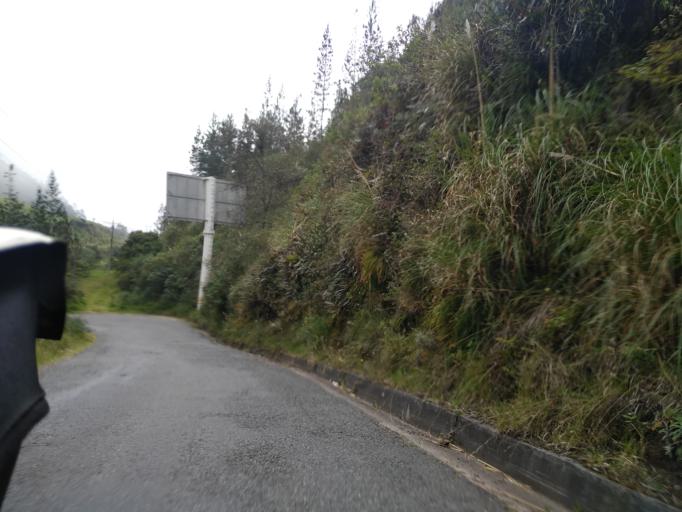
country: EC
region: Cotopaxi
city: Saquisili
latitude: -0.6975
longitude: -78.8107
